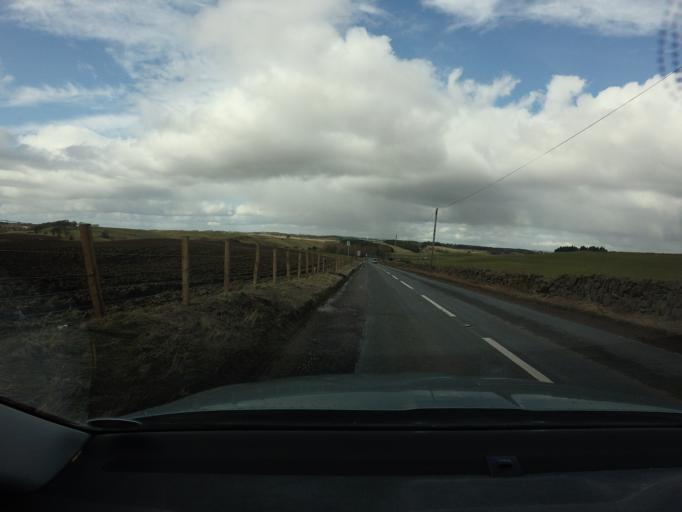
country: GB
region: Scotland
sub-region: South Lanarkshire
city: Lanark
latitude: 55.6368
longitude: -3.7416
